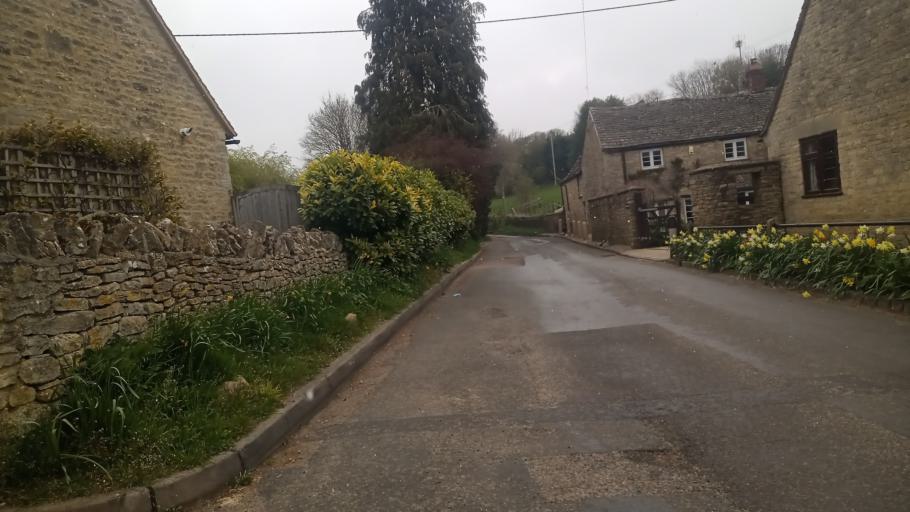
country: GB
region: England
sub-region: Oxfordshire
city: Witney
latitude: 51.8069
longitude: -1.5057
